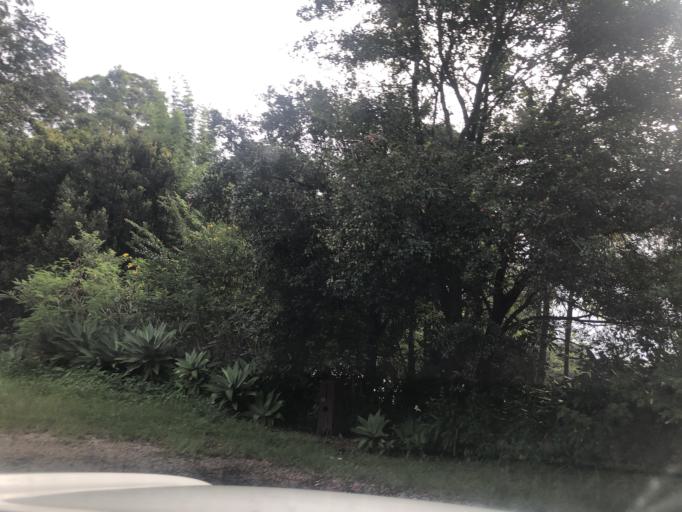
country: AU
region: New South Wales
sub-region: Bellingen
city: Bellingen
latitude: -30.4623
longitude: 152.9019
